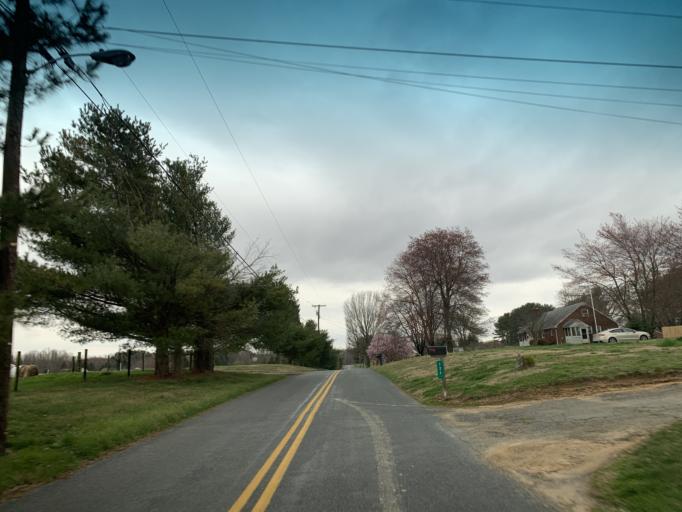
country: US
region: Maryland
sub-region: Harford County
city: Aberdeen
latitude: 39.5753
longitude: -76.1976
